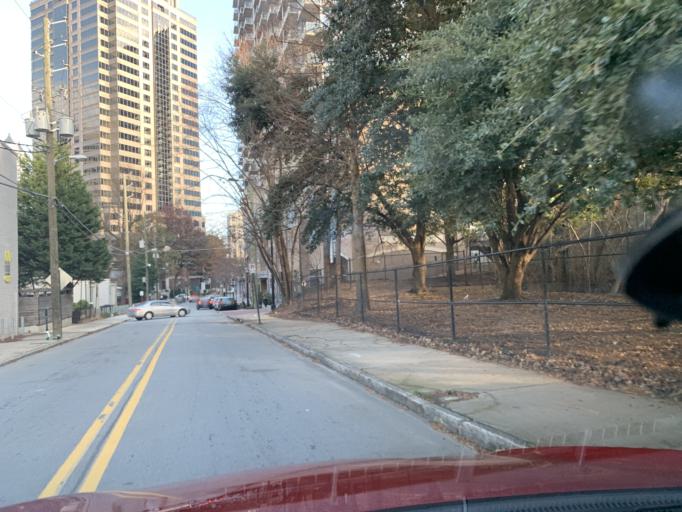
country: US
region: Georgia
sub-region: Fulton County
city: Atlanta
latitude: 33.7849
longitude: -84.3856
